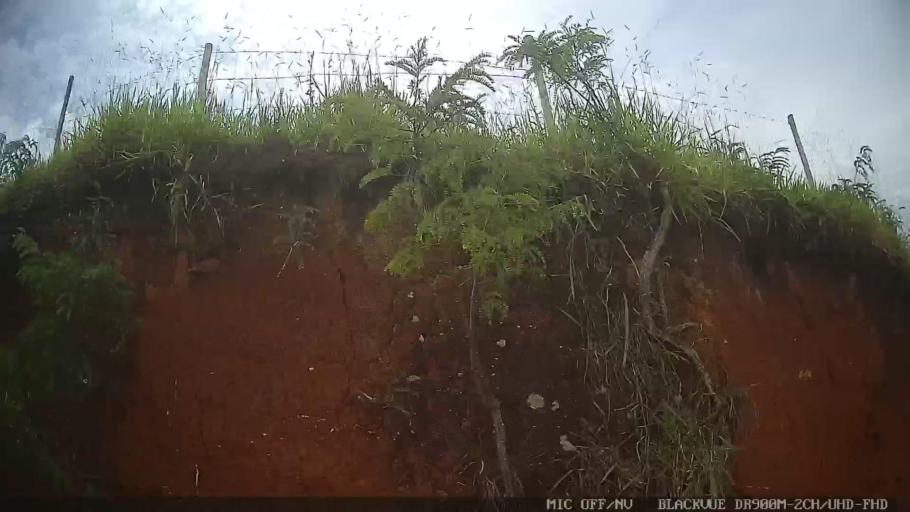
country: BR
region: Sao Paulo
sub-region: Santa Isabel
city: Santa Isabel
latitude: -23.3450
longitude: -46.2277
